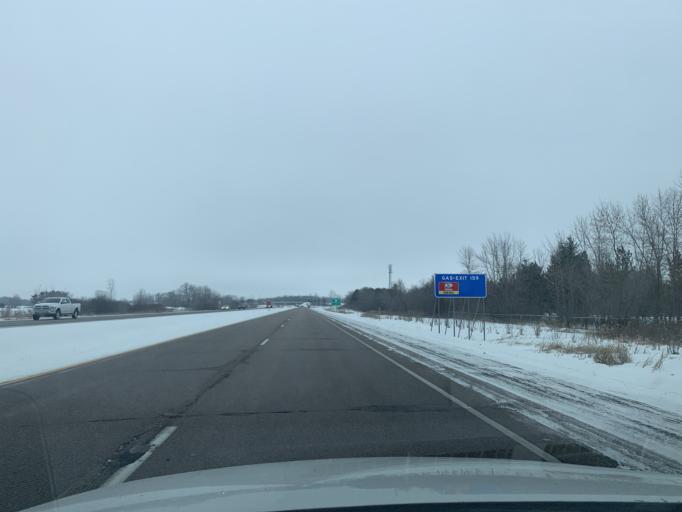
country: US
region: Minnesota
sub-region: Chisago County
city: Rush City
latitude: 45.6769
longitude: -92.9913
